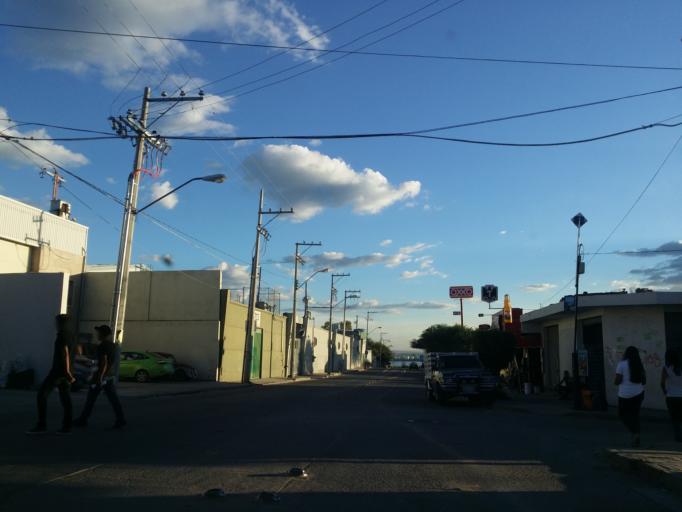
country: MX
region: Guanajuato
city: Leon
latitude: 21.2024
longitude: -101.6778
